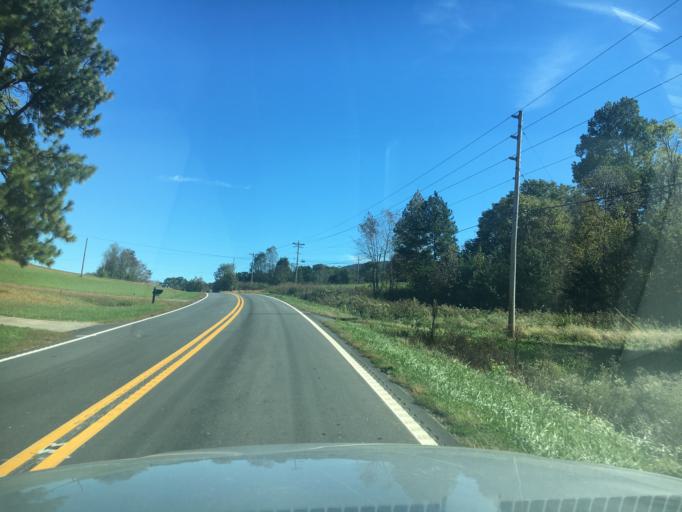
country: US
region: North Carolina
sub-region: Burke County
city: Glen Alpine
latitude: 35.6426
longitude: -81.7753
